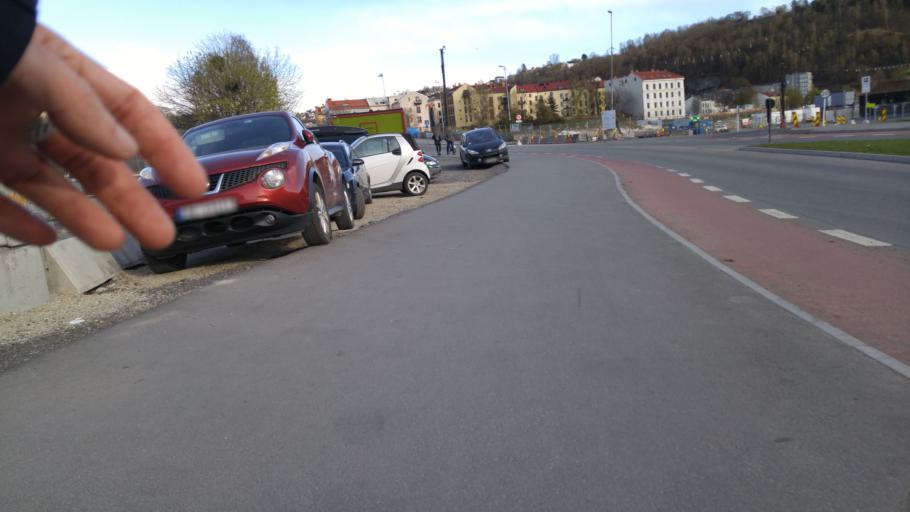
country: NO
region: Oslo
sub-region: Oslo
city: Oslo
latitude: 59.9067
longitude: 10.7629
